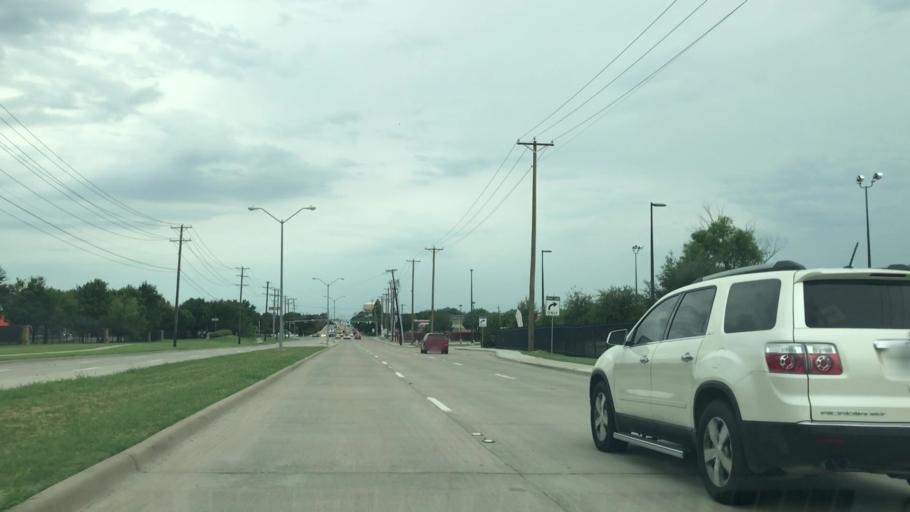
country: US
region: Texas
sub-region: Dallas County
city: Richardson
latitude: 32.9977
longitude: -96.7642
